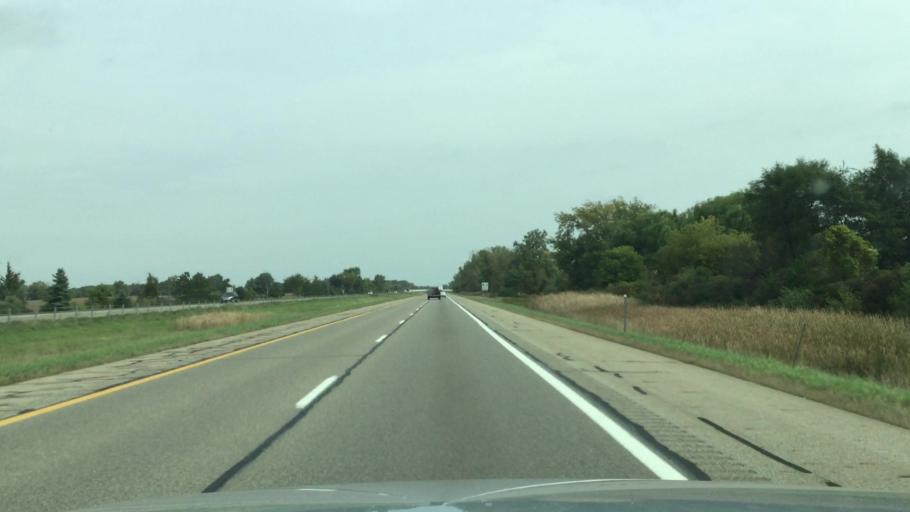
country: US
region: Michigan
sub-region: Shiawassee County
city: Durand
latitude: 42.9409
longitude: -83.9829
